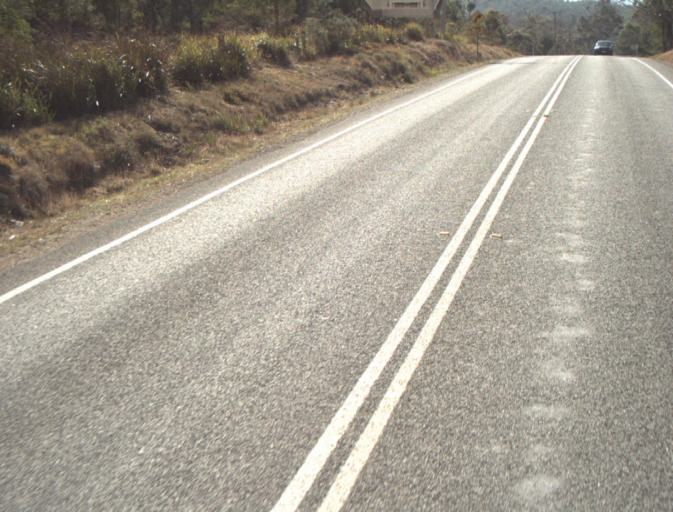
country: AU
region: Tasmania
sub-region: Launceston
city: Mayfield
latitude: -41.3473
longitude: 147.1417
